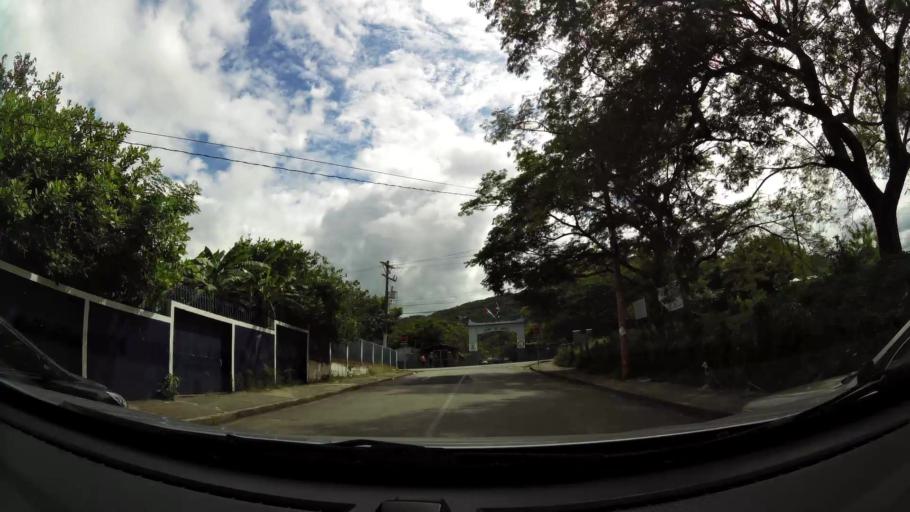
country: CR
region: Guanacaste
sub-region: Canton de Nicoya
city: Nicoya
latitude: 10.1406
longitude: -85.4523
